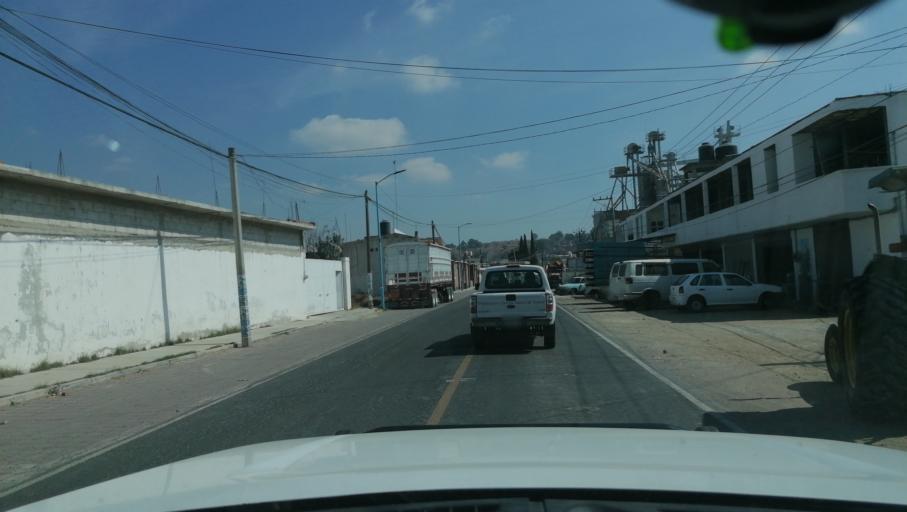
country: MX
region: Tlaxcala
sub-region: Tetlatlahuca
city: Santa Cruz Aquiahuac
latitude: 19.2355
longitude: -98.2837
